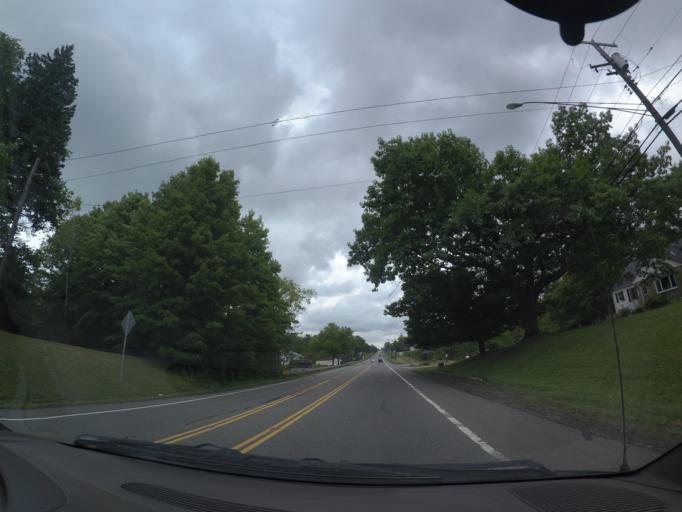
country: US
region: Ohio
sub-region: Ashtabula County
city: Geneva
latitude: 41.7832
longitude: -80.9467
